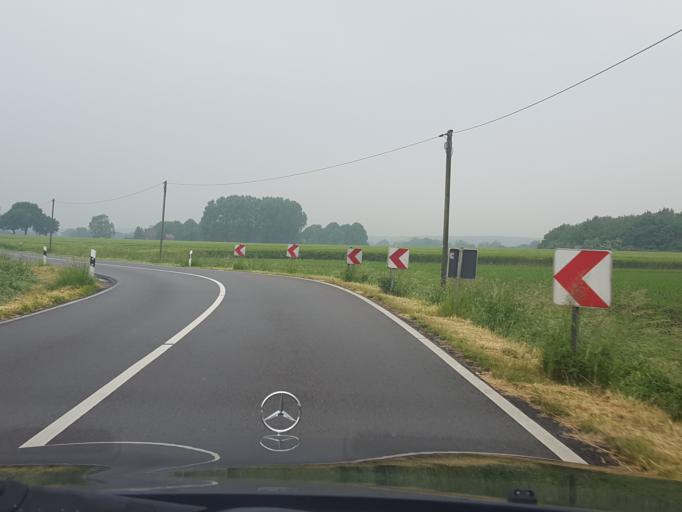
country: DE
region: North Rhine-Westphalia
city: Oer-Erkenschwick
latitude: 51.6359
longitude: 7.2419
